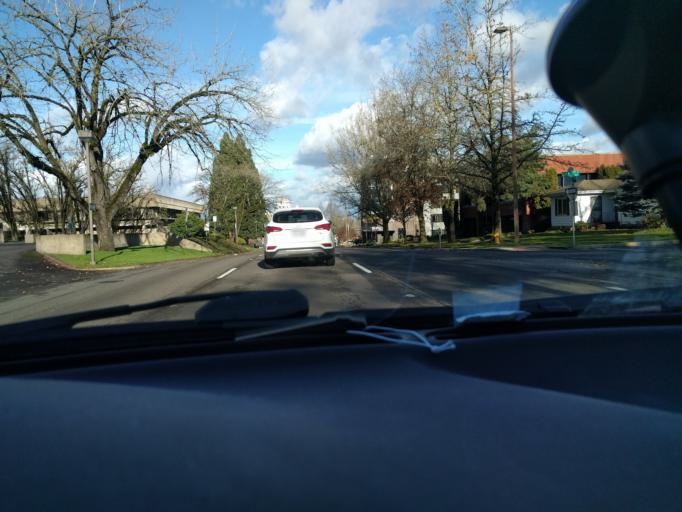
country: US
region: Oregon
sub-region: Marion County
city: Salem
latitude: 44.9349
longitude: -123.0416
